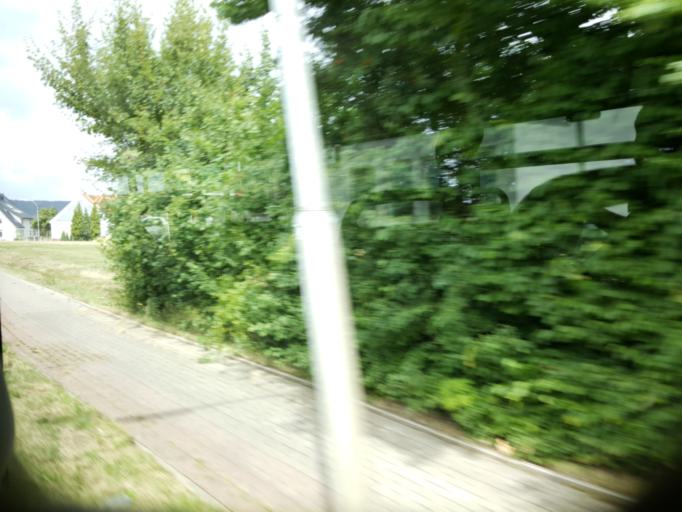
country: DE
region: North Rhine-Westphalia
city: Bad Oeynhausen
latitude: 52.2237
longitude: 8.8204
